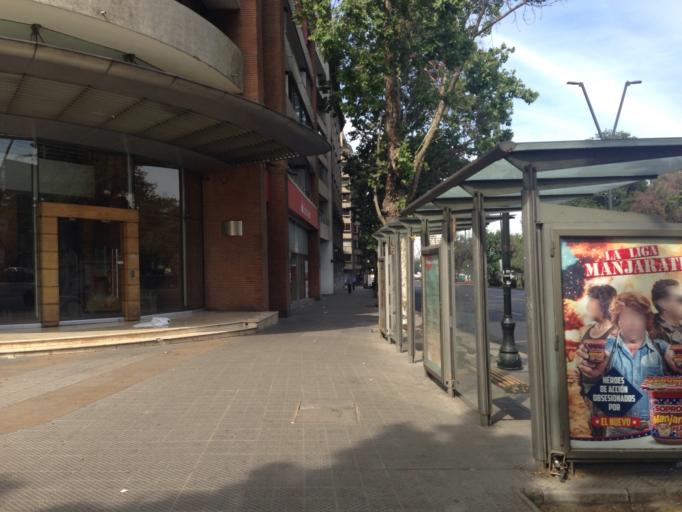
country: CL
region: Santiago Metropolitan
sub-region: Provincia de Santiago
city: Santiago
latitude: -33.4347
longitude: -70.6276
